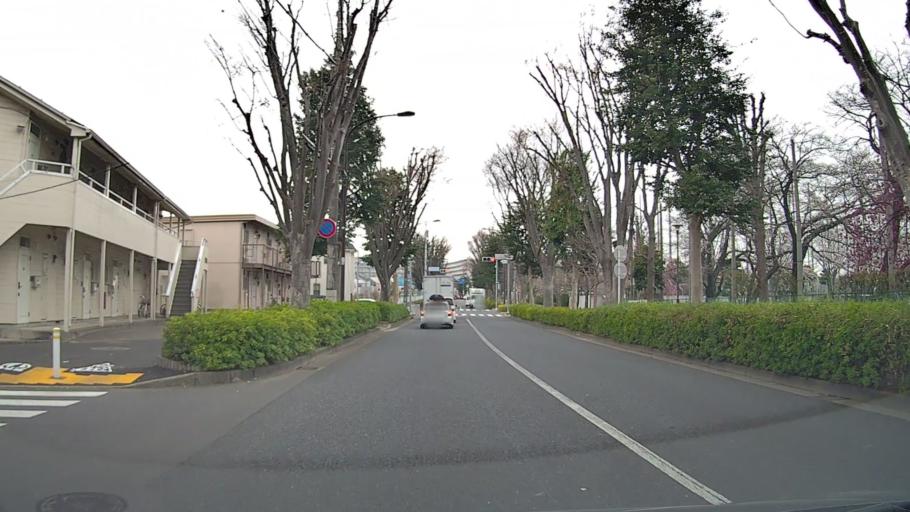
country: JP
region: Saitama
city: Asaka
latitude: 35.7763
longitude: 139.5907
